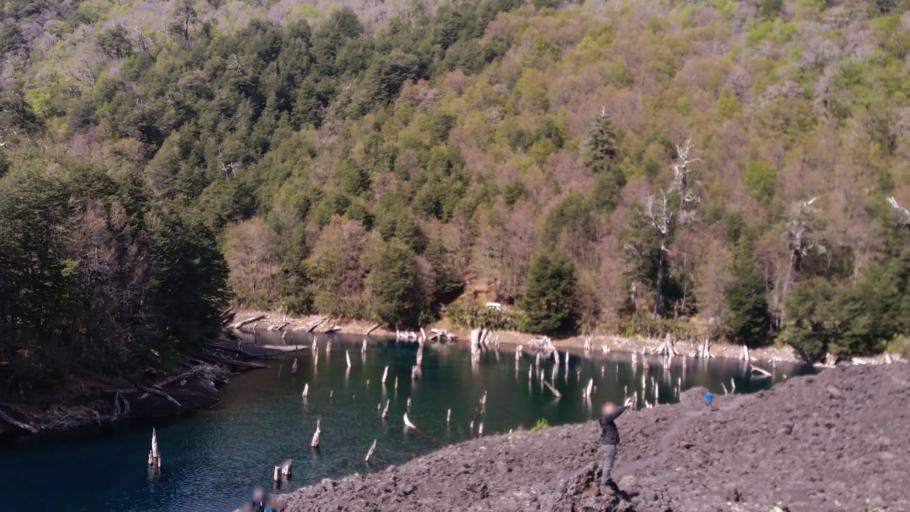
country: CL
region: Araucania
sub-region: Provincia de Cautin
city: Vilcun
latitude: -38.6720
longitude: -71.6231
